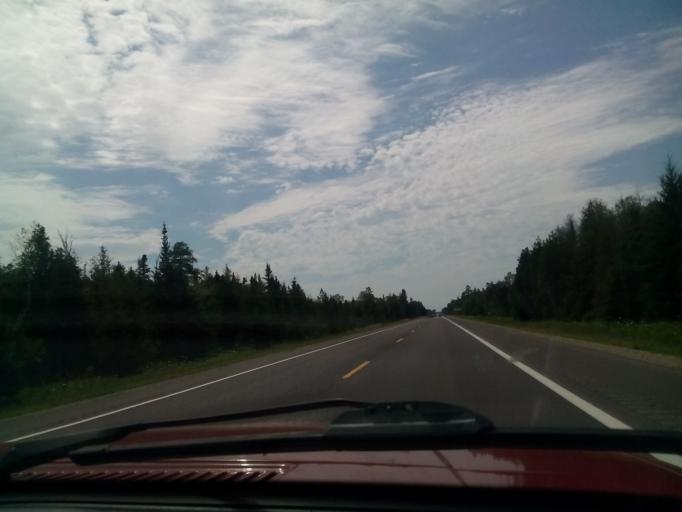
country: US
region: Michigan
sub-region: Schoolcraft County
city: Manistique
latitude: 46.0325
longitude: -85.9791
